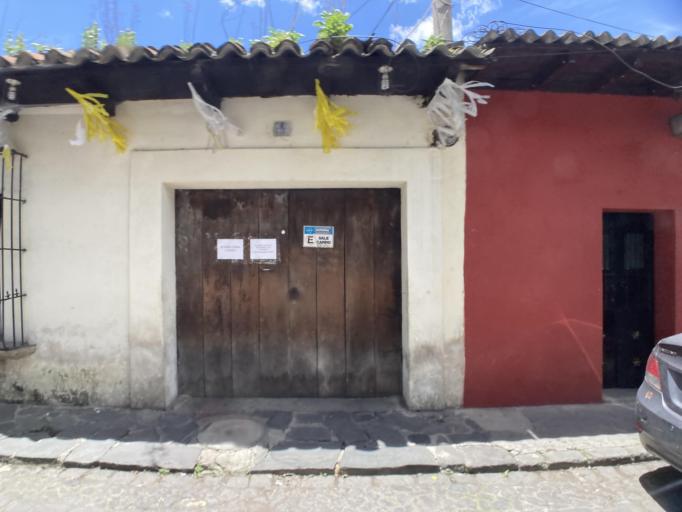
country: GT
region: Sacatepequez
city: Antigua Guatemala
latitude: 14.5509
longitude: -90.7311
